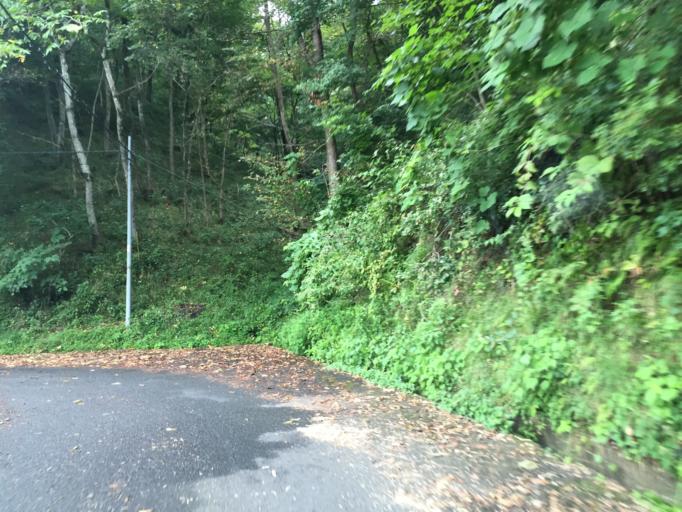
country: JP
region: Fukushima
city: Fukushima-shi
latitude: 37.8042
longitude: 140.3568
